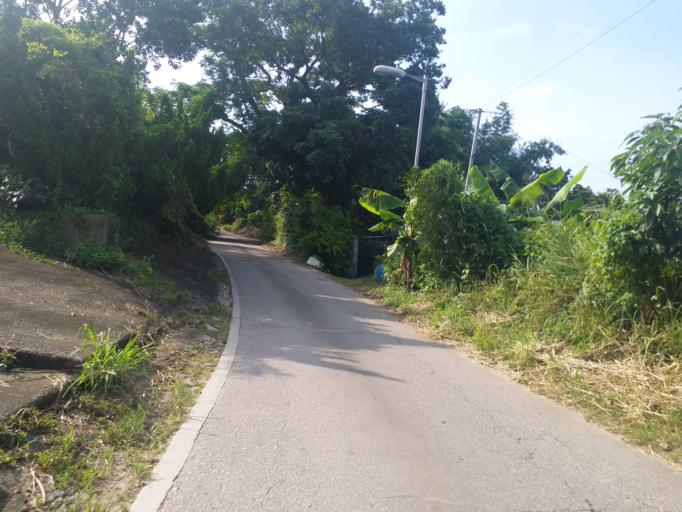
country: HK
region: Yuen Long
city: Yuen Long Kau Hui
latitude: 22.4454
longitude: 114.0112
